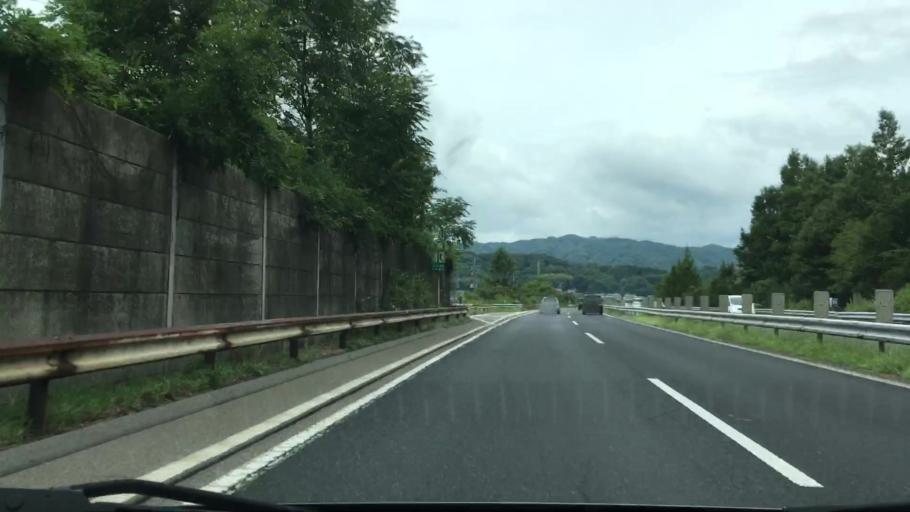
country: JP
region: Okayama
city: Tsuyama
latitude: 35.0576
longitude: 133.9254
